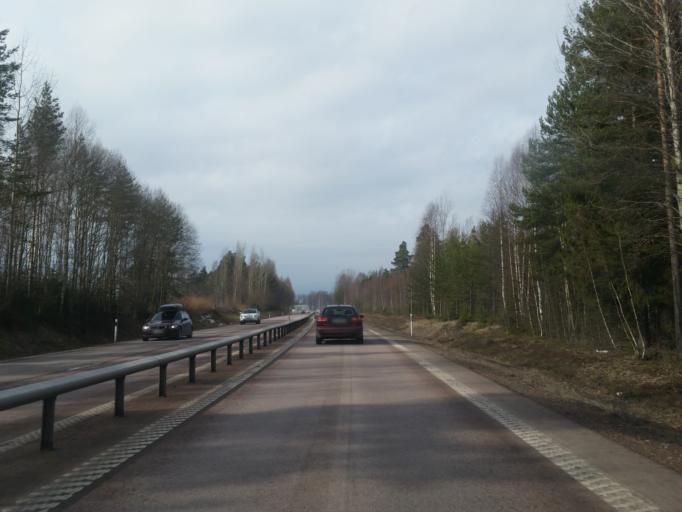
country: SE
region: Dalarna
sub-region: Mora Kommun
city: Mora
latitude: 61.0074
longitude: 14.6178
